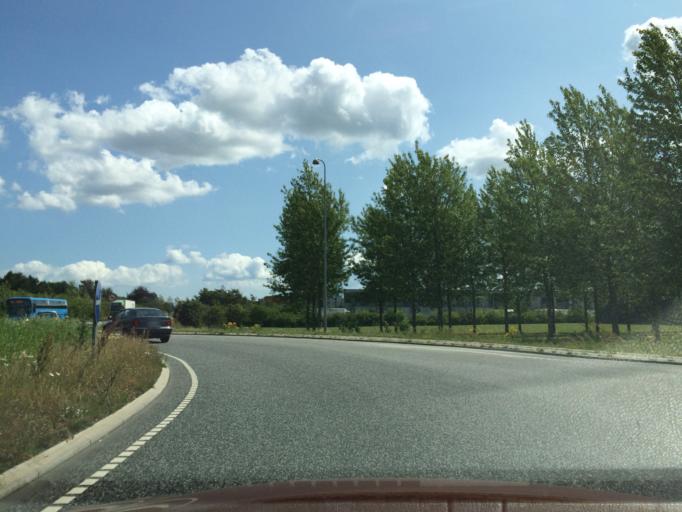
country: DK
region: Central Jutland
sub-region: Favrskov Kommune
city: Soften
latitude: 56.1868
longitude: 10.0875
